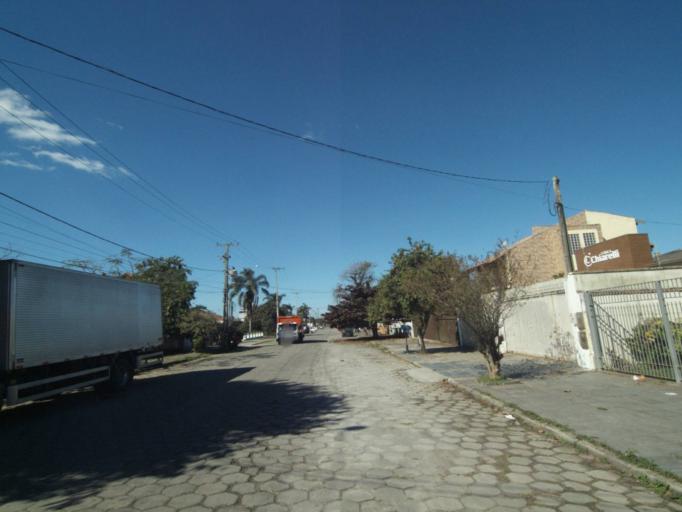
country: BR
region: Parana
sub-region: Paranagua
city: Paranagua
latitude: -25.5114
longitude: -48.5061
